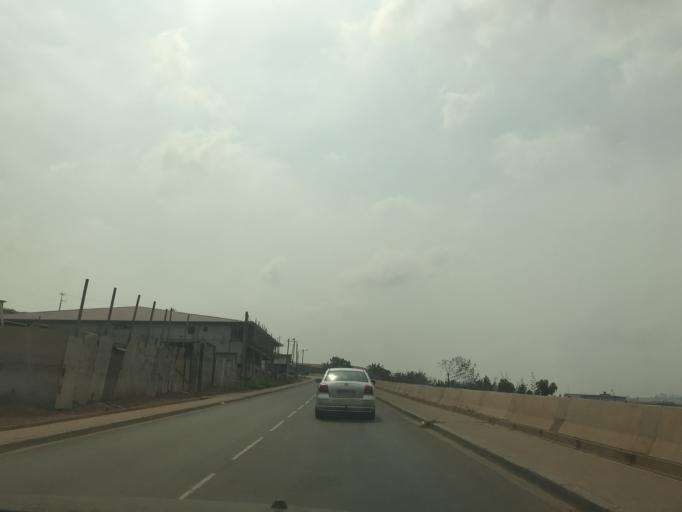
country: CM
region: Centre
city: Yaounde
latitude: 3.8232
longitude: 11.5128
